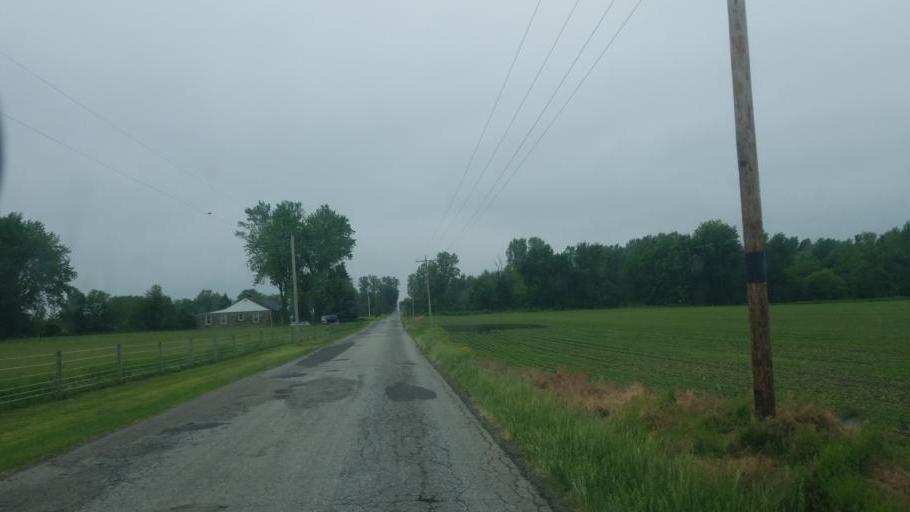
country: US
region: Indiana
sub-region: Marshall County
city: Bremen
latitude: 41.4661
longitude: -86.1177
